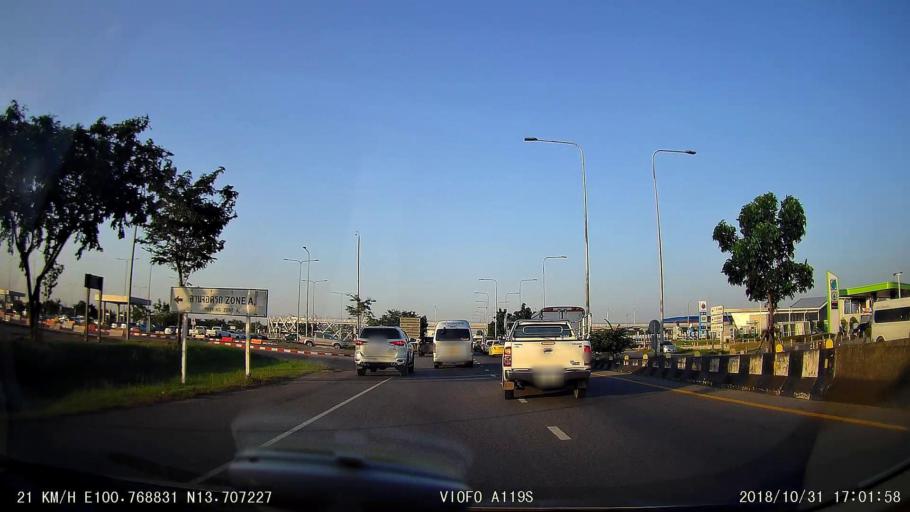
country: TH
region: Bangkok
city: Lat Krabang
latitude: 13.7071
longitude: 100.7688
